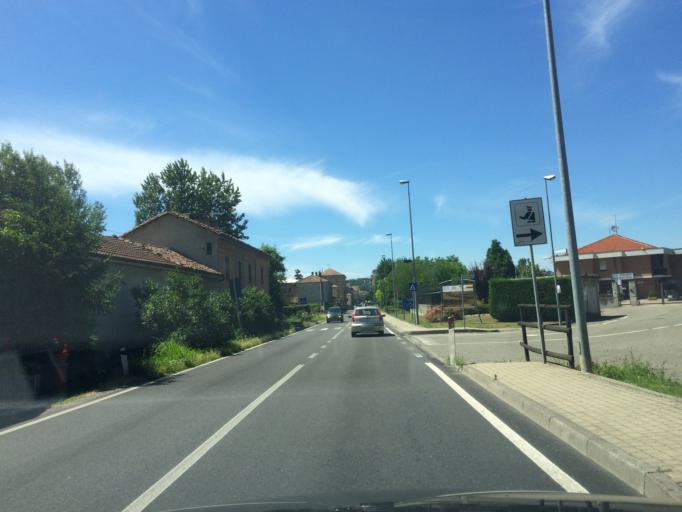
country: IT
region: Piedmont
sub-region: Provincia di Asti
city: Nizza Monferrato
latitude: 44.7680
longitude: 8.3680
